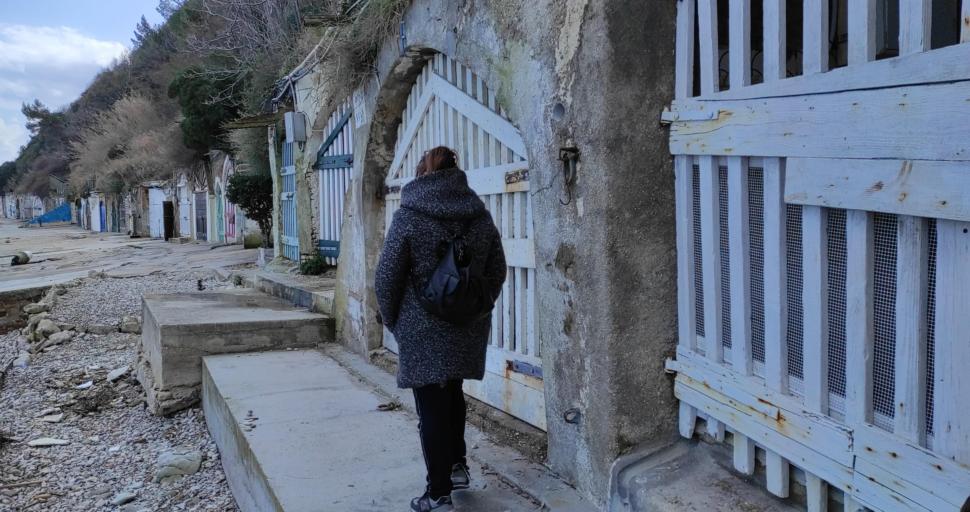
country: IT
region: The Marches
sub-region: Provincia di Ancona
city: Pietra la Croce
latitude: 43.6186
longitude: 13.5316
